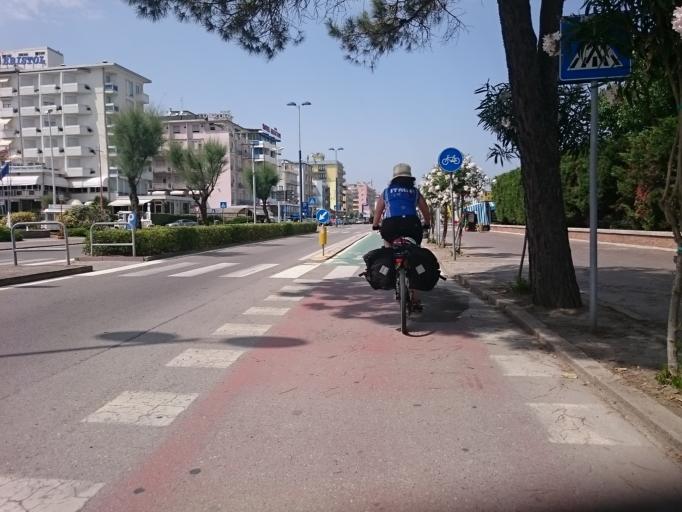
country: IT
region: Veneto
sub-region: Provincia di Venezia
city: Chioggia
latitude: 45.2121
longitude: 12.2954
